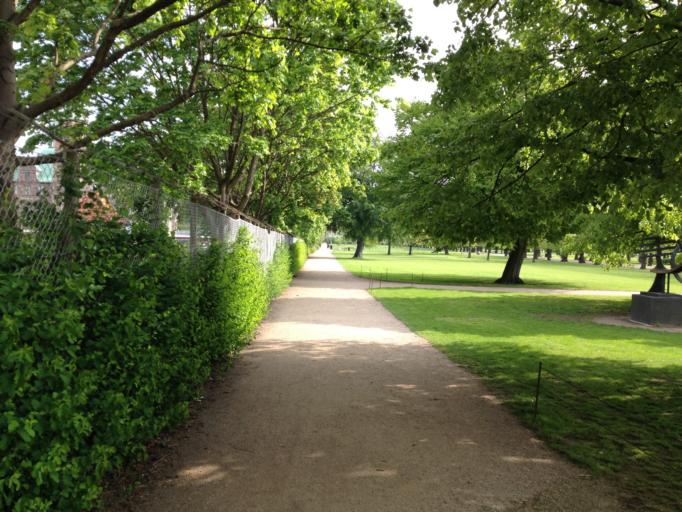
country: DK
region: Capital Region
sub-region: Kobenhavn
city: Copenhagen
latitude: 55.6841
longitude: 12.5766
